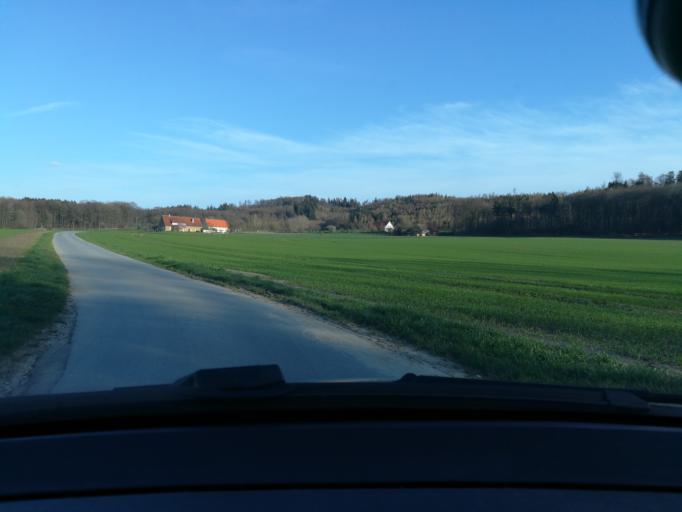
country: DE
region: North Rhine-Westphalia
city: Borgholzhausen
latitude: 52.0927
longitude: 8.3035
